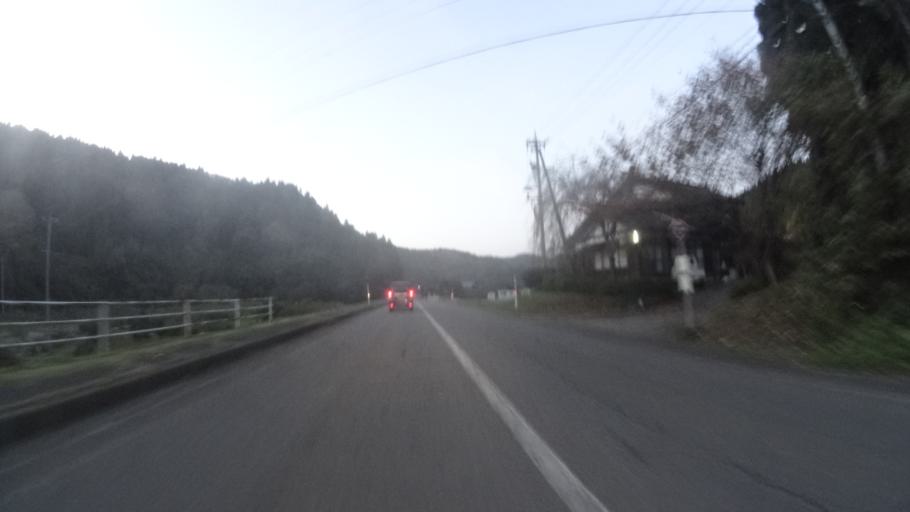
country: JP
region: Ishikawa
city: Nanao
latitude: 37.3567
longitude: 136.8670
